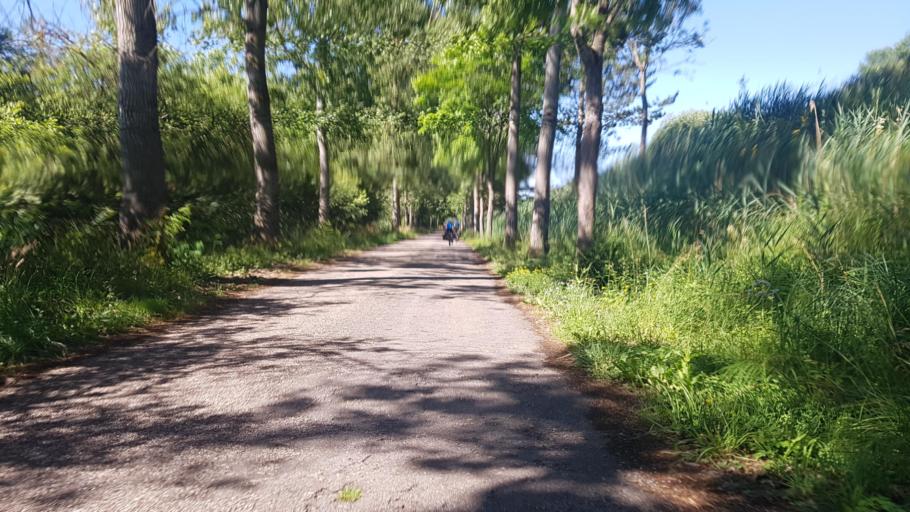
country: FR
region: Lorraine
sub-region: Departement de Meurthe-et-Moselle
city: Einville-au-Jard
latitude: 48.6619
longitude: 6.4984
